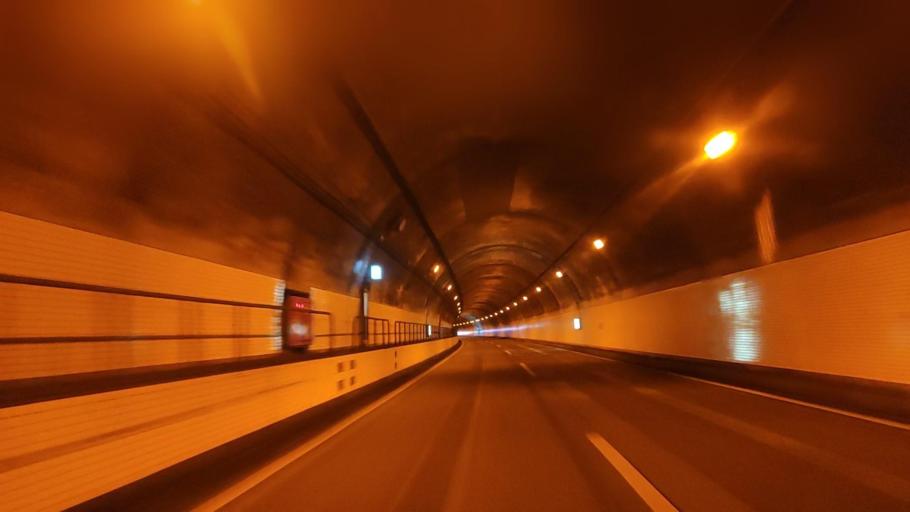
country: JP
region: Niigata
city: Itoigawa
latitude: 37.0186
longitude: 137.8366
